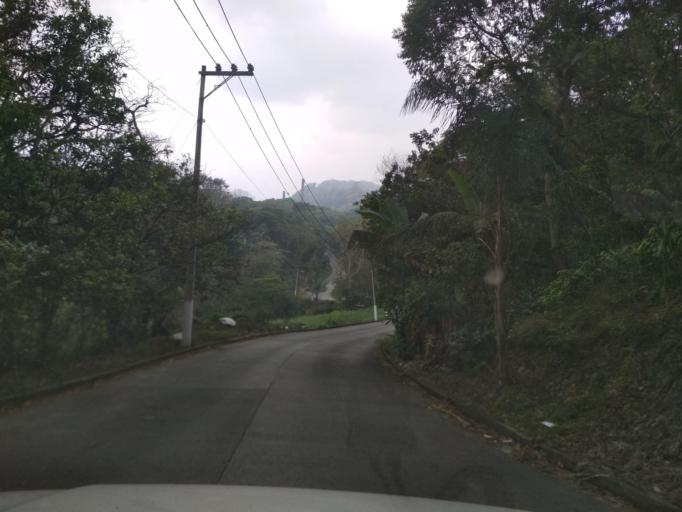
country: MX
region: Veracruz
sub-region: Cordoba
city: San Jose de Tapia
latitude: 18.8394
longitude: -96.9842
